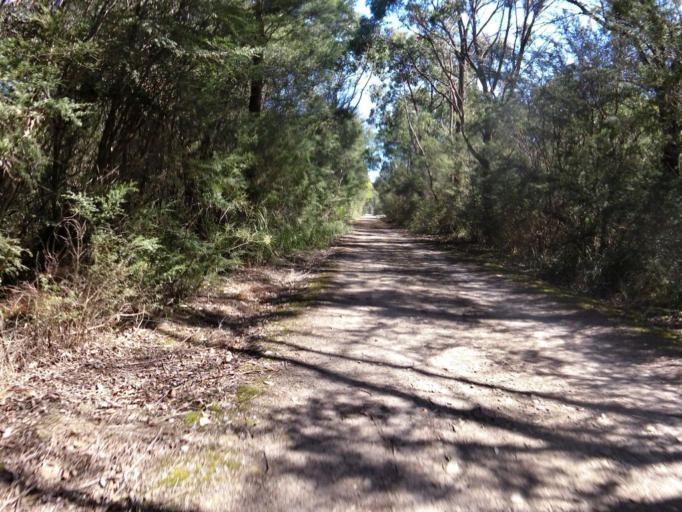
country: AU
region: Victoria
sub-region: Latrobe
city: Moe
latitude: -38.1704
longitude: 146.3064
